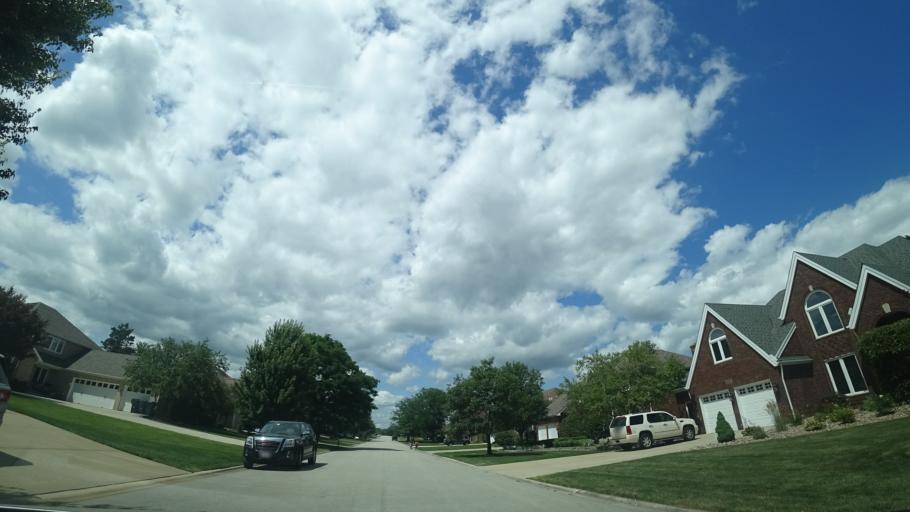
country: US
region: Illinois
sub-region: Will County
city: Homer Glen
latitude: 41.5802
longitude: -87.9141
